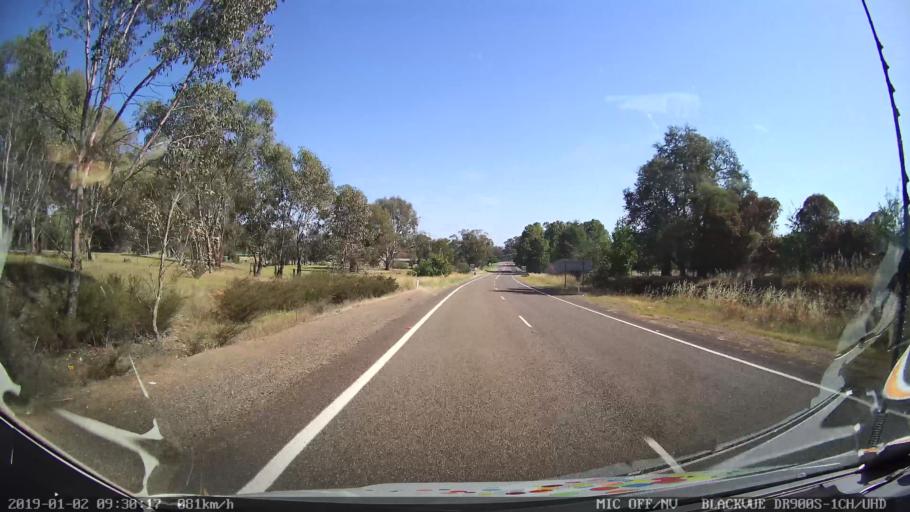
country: AU
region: New South Wales
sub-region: Tumut Shire
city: Tumut
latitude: -35.3284
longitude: 148.2376
